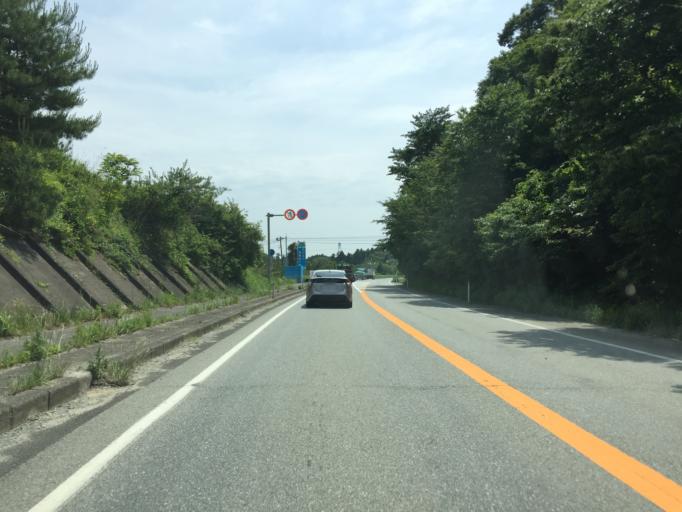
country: JP
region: Fukushima
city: Namie
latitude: 37.4365
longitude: 141.0113
